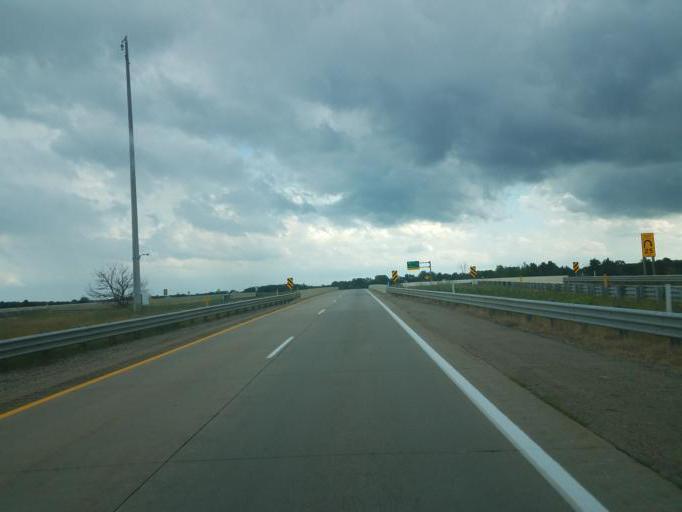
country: US
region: Michigan
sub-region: Calhoun County
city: Marshall
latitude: 42.2984
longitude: -84.9968
